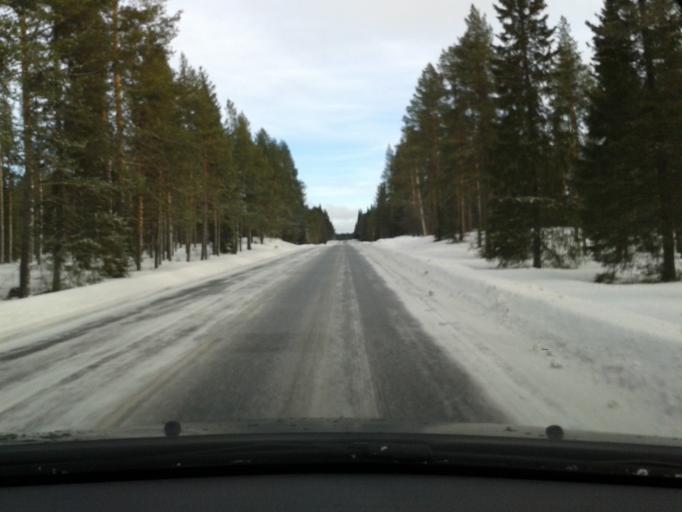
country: SE
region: Vaesterbotten
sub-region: Vilhelmina Kommun
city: Vilhelmina
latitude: 64.6425
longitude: 16.4851
